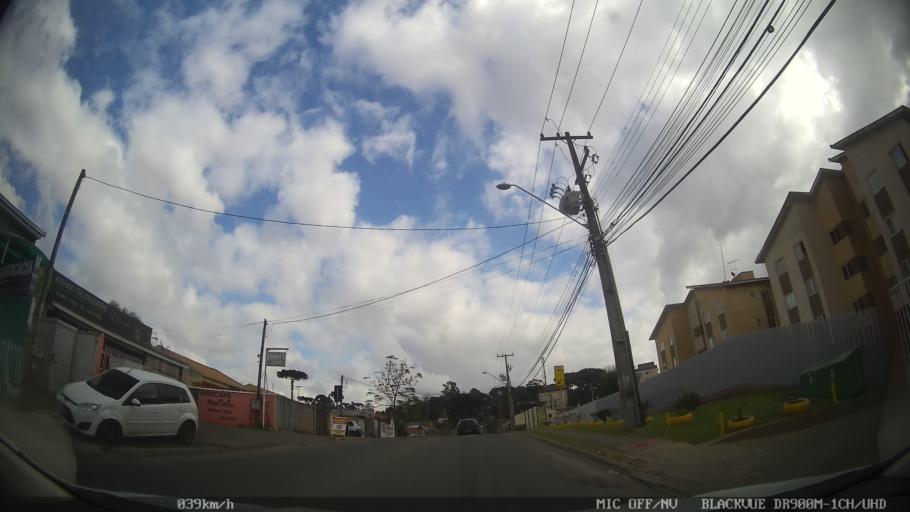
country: BR
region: Parana
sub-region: Colombo
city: Colombo
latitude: -25.3461
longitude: -49.1972
